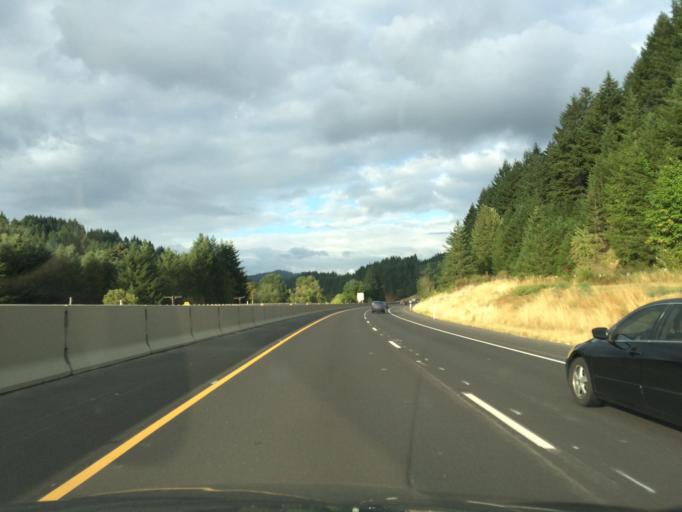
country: US
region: Oregon
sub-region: Douglas County
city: Drain
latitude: 43.7346
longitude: -123.1956
